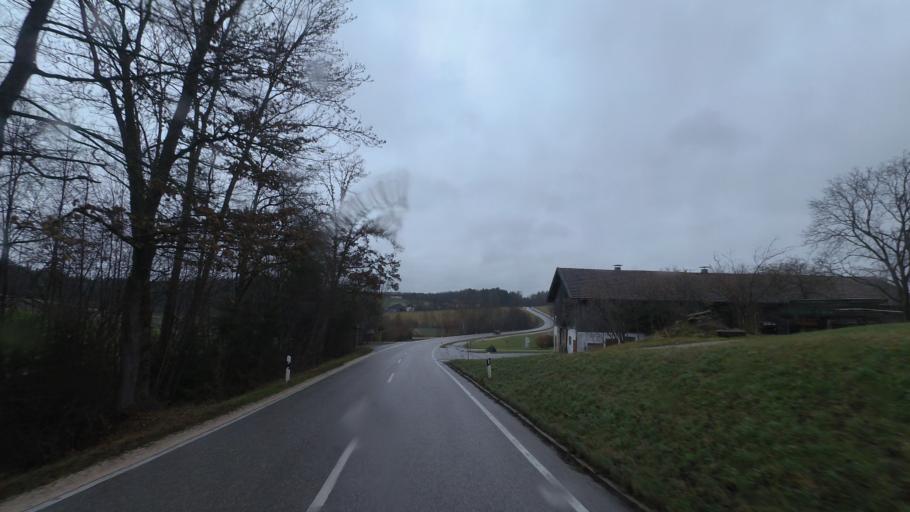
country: DE
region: Bavaria
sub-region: Upper Bavaria
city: Kirchanschoring
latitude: 47.9461
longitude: 12.8159
